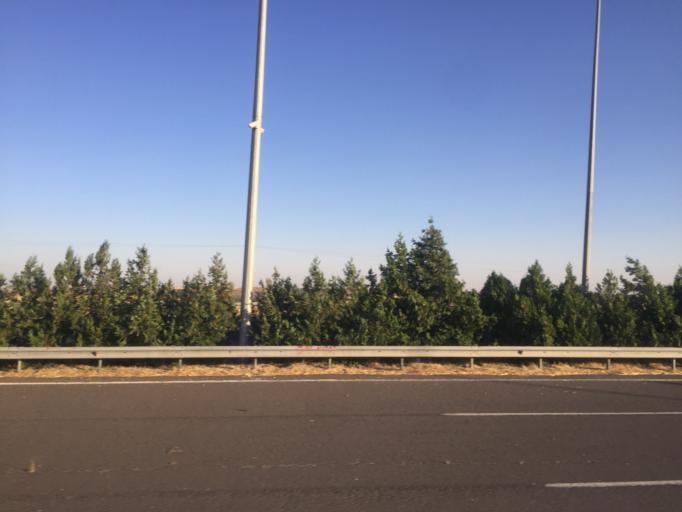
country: TR
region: Sanliurfa
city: Bogurtlen
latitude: 37.1001
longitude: 38.1964
